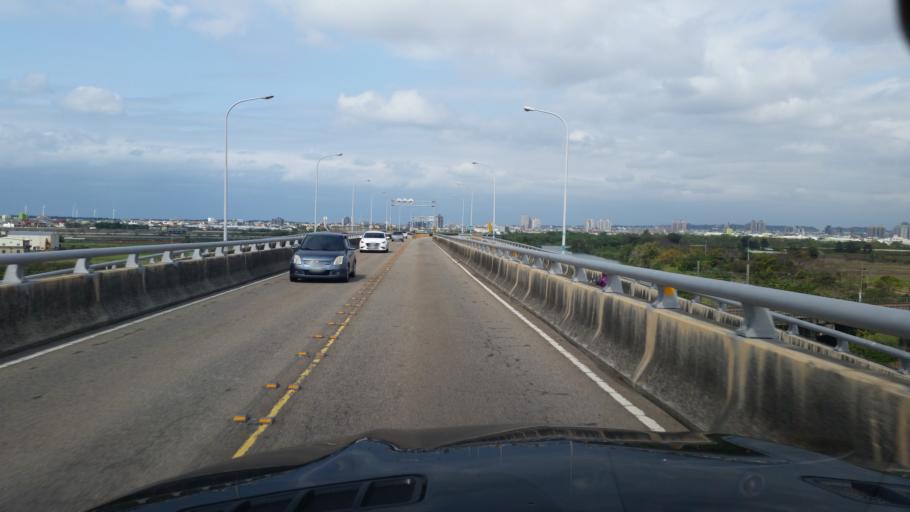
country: TW
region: Taiwan
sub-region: Miaoli
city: Miaoli
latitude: 24.6583
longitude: 120.8668
